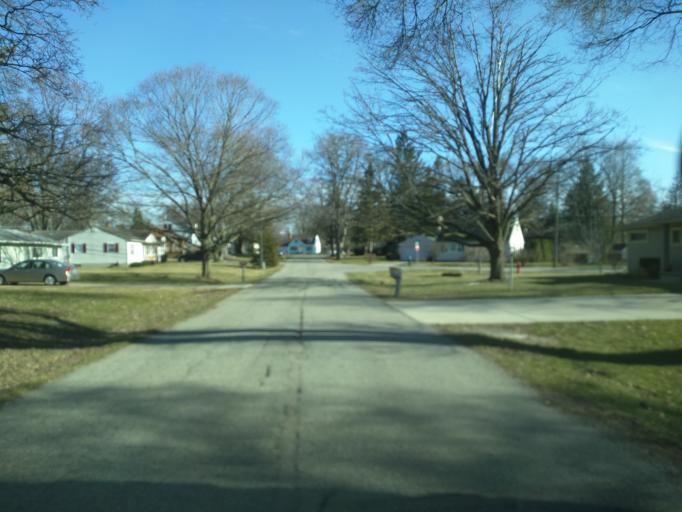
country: US
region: Michigan
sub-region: Ingham County
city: Edgemont Park
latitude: 42.7638
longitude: -84.5842
